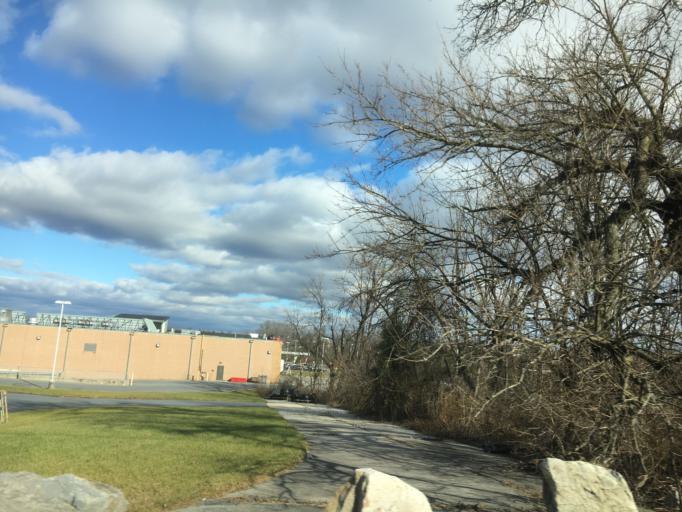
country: US
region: Pennsylvania
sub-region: Lehigh County
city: Stiles
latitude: 40.6618
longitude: -75.5135
